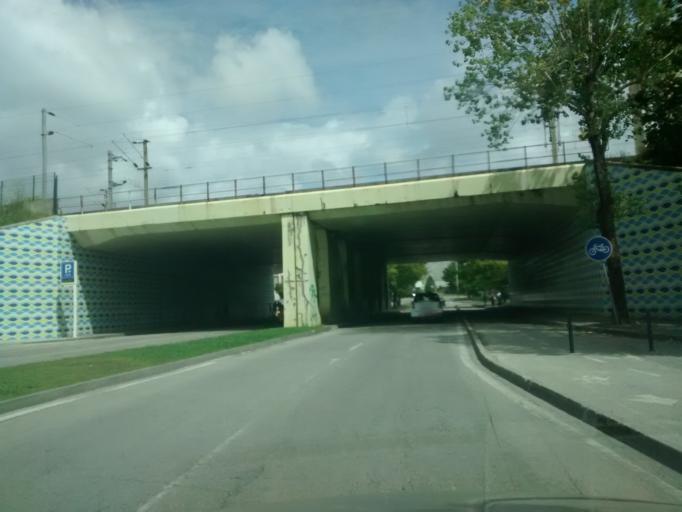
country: PT
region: Aveiro
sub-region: Aveiro
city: Aveiro
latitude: 40.6408
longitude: -8.6423
